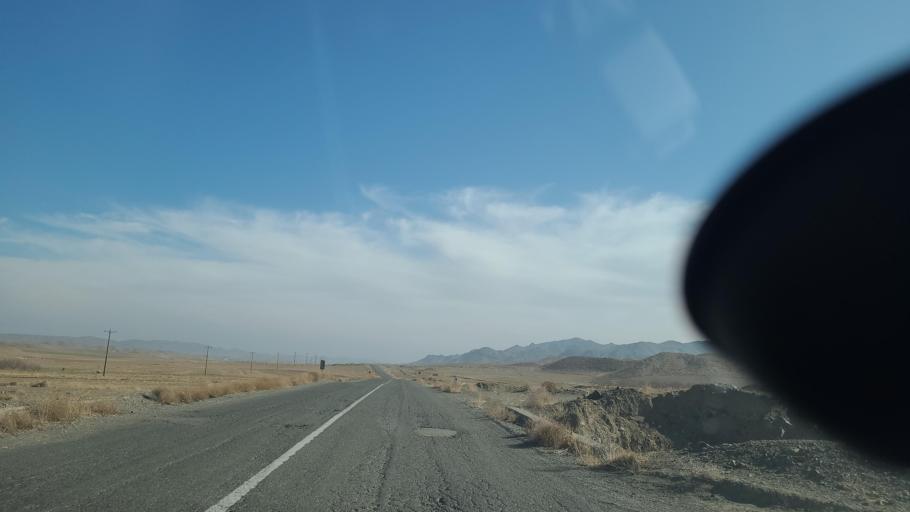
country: IR
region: Razavi Khorasan
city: Fariman
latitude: 35.5876
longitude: 59.6396
